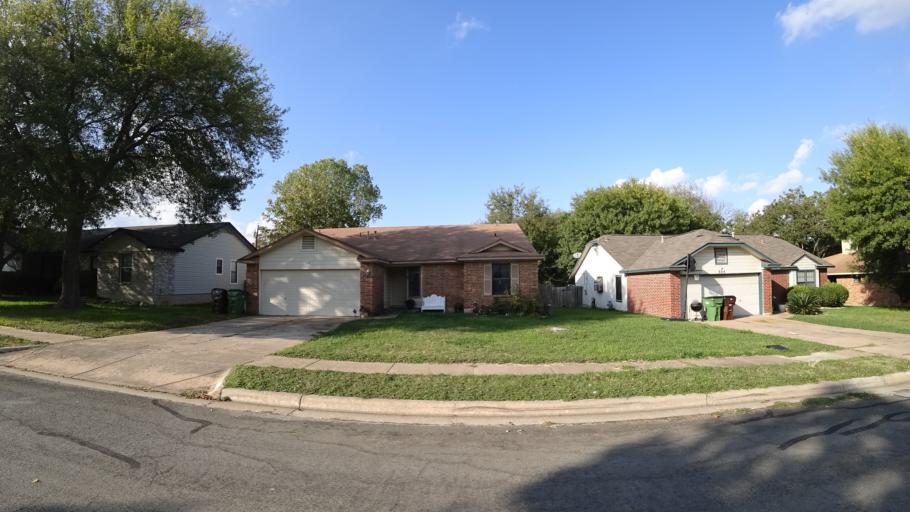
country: US
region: Texas
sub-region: Williamson County
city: Round Rock
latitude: 30.4913
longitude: -97.6700
